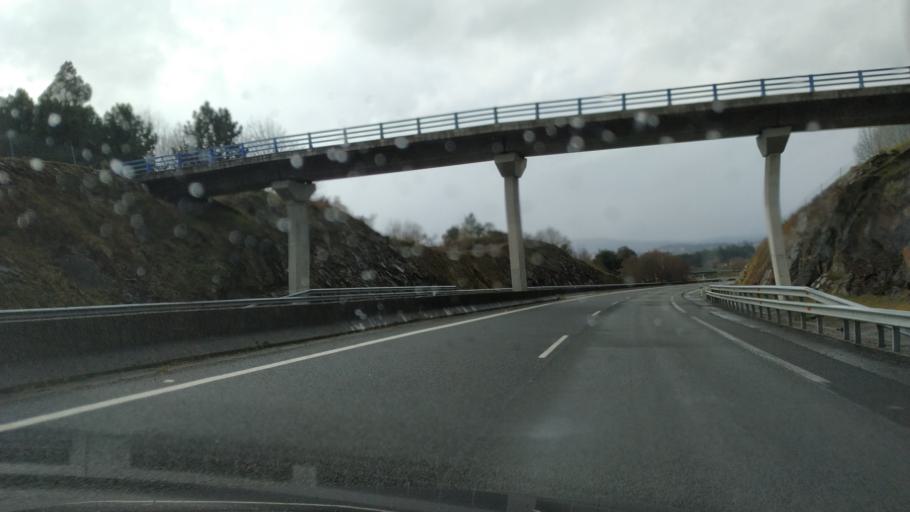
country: ES
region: Galicia
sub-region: Provincia de Pontevedra
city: Silleda
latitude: 42.7161
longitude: -8.2560
